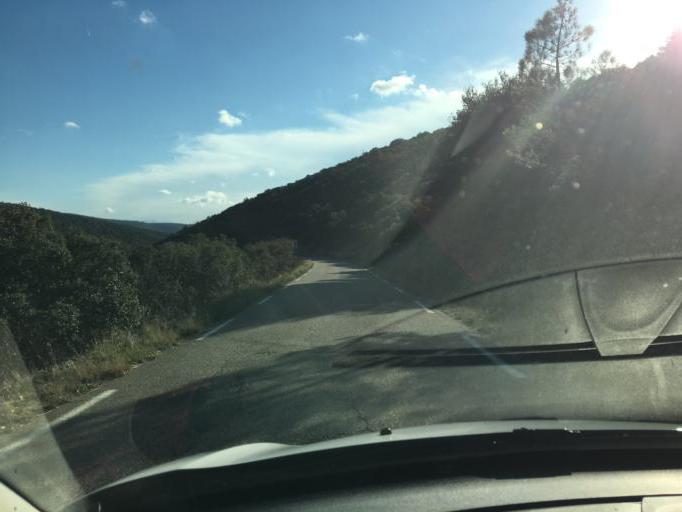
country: FR
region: Provence-Alpes-Cote d'Azur
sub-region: Departement du Vaucluse
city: Villes-sur-Auzon
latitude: 44.0392
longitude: 5.2672
